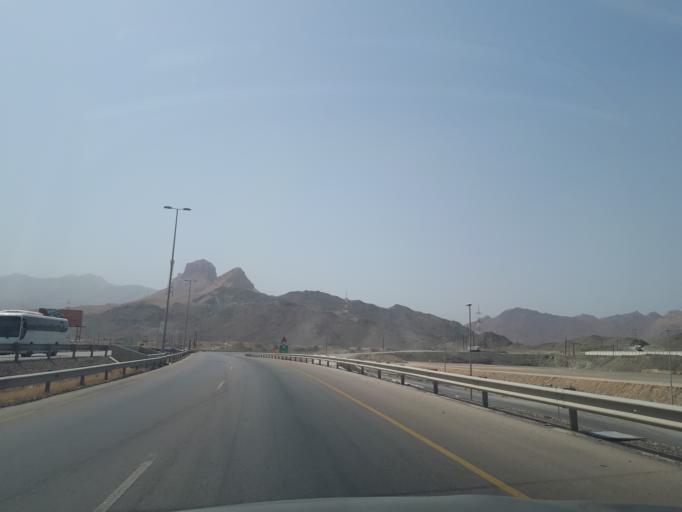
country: OM
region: Muhafazat ad Dakhiliyah
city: Bidbid
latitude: 23.4851
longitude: 58.1976
